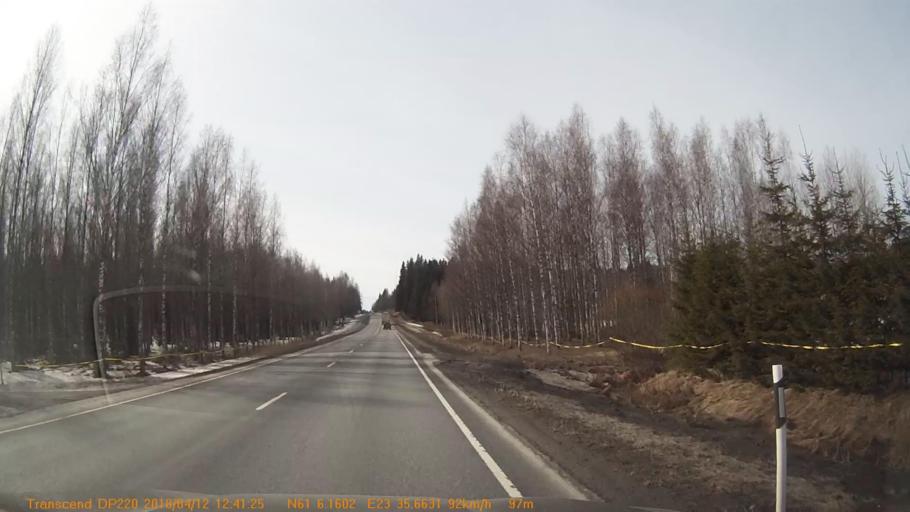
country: FI
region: Pirkanmaa
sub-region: Etelae-Pirkanmaa
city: Urjala
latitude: 61.1026
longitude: 23.5939
